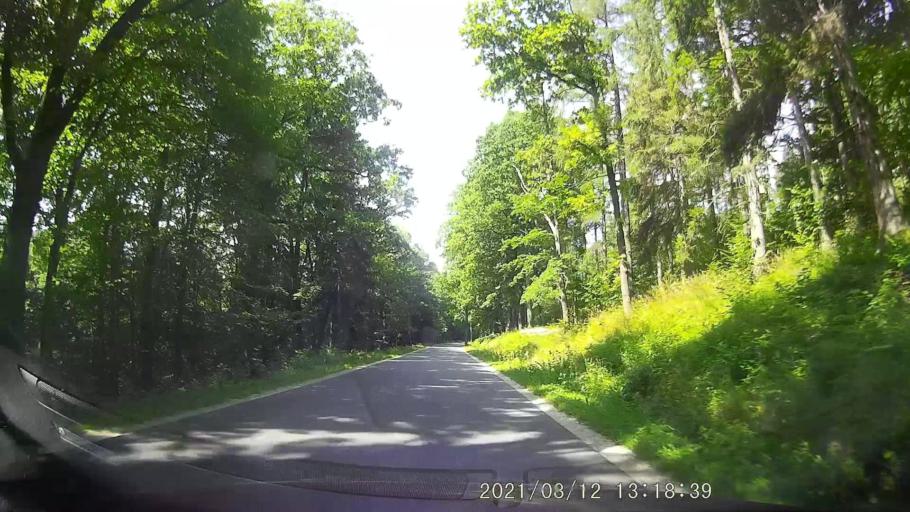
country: PL
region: Lower Silesian Voivodeship
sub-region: Powiat klodzki
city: Stronie Slaskie
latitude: 50.2731
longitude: 16.8897
